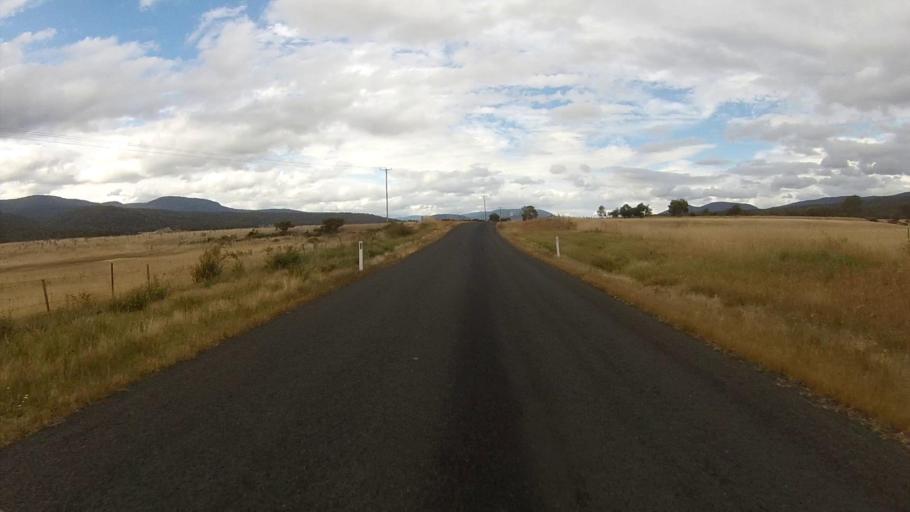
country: AU
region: Tasmania
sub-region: Break O'Day
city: St Helens
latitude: -41.8233
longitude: 147.8712
